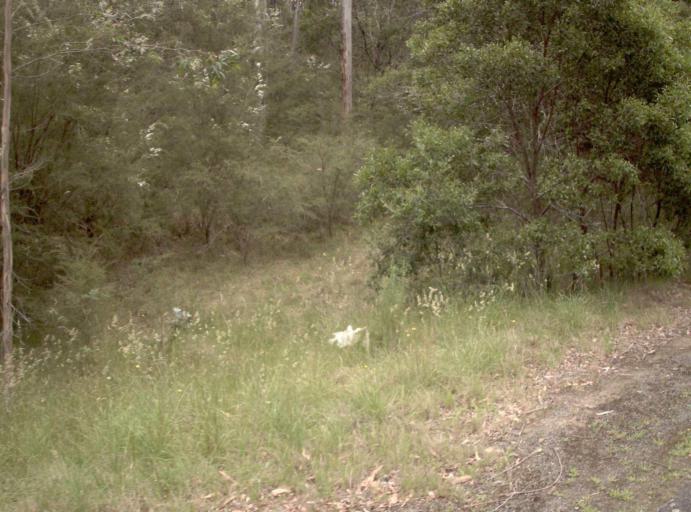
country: AU
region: New South Wales
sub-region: Bombala
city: Bombala
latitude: -37.2872
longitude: 149.2223
